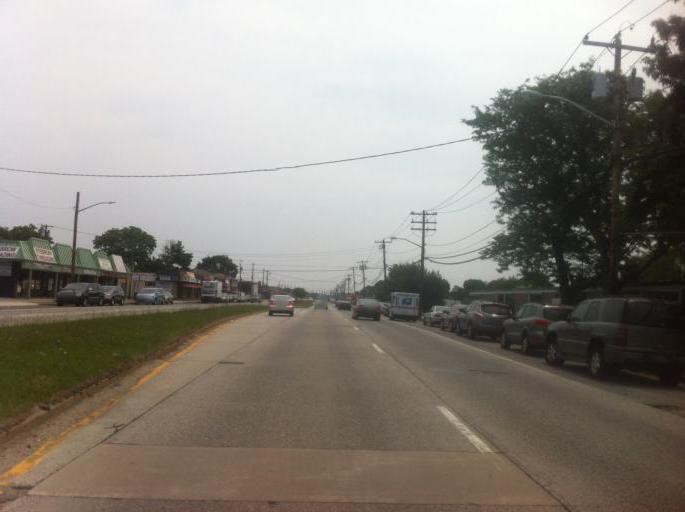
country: US
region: New York
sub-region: Nassau County
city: Hicksville
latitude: 40.7615
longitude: -73.5164
